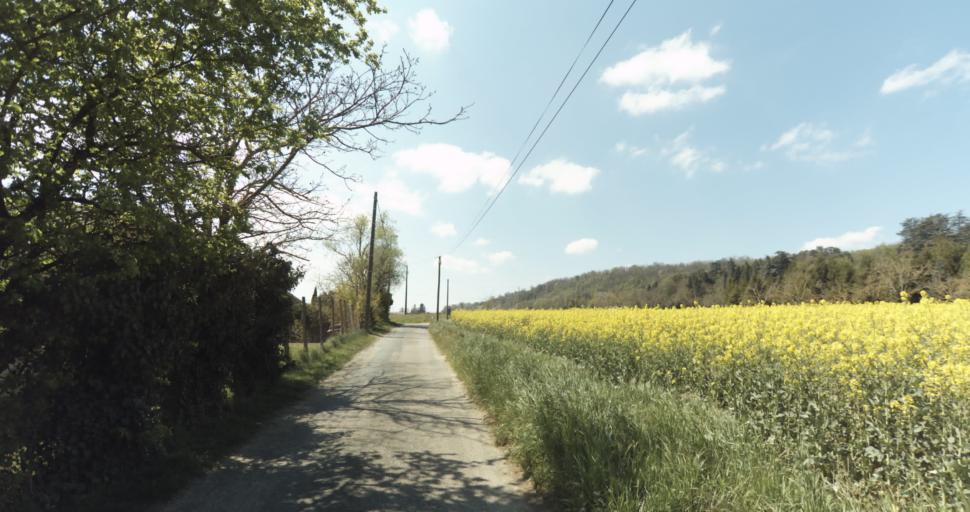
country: FR
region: Rhone-Alpes
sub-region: Departement de l'Isere
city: Saint-Marcellin
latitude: 45.1501
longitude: 5.3049
